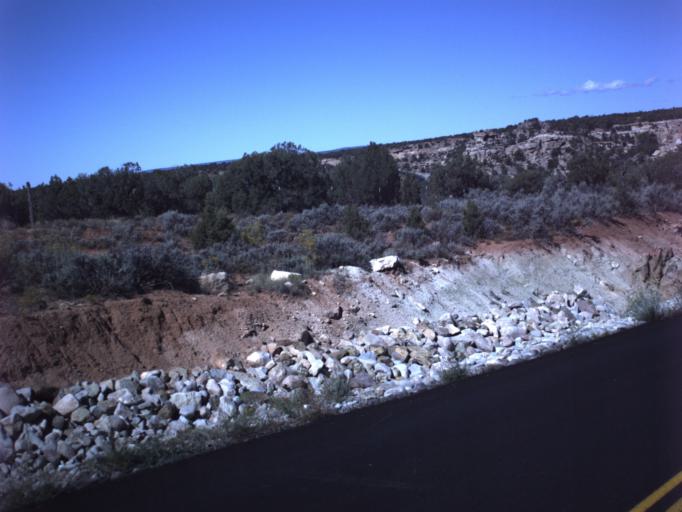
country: US
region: Utah
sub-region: San Juan County
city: Blanding
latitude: 37.5759
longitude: -109.5042
